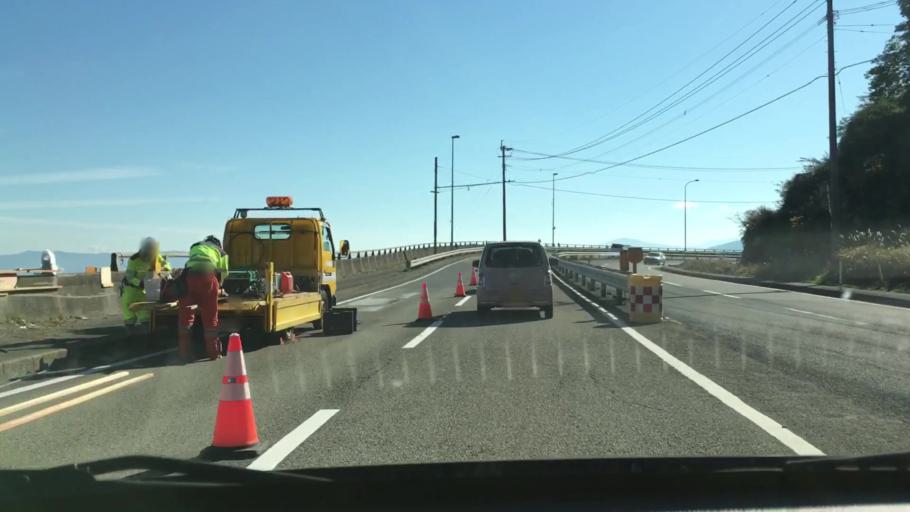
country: JP
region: Kagoshima
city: Kajiki
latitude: 31.6594
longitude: 130.6183
